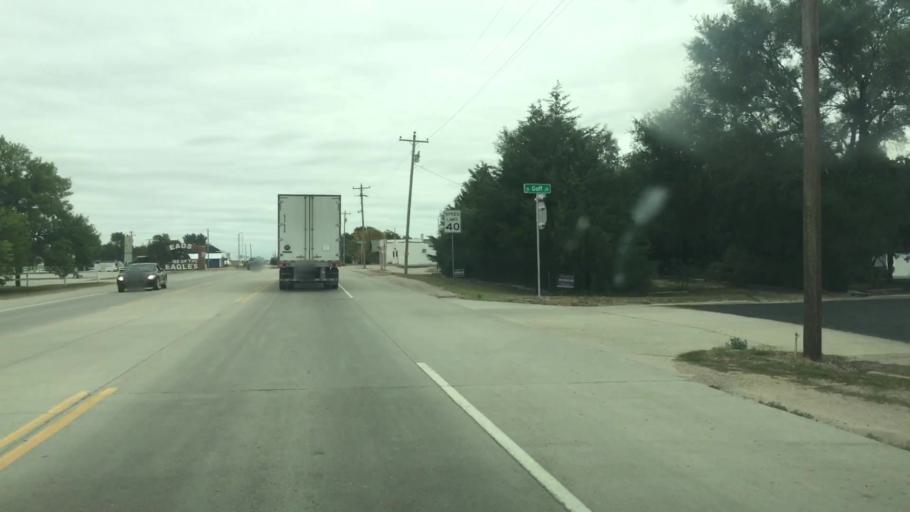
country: US
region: Colorado
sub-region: Kiowa County
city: Eads
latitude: 38.4777
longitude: -102.7805
